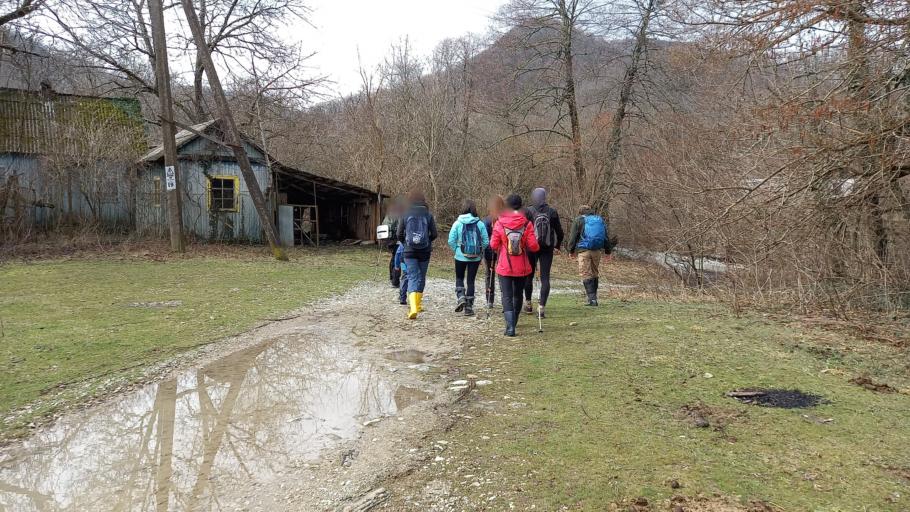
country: RU
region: Krasnodarskiy
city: Dzhubga
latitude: 44.4114
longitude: 38.7181
